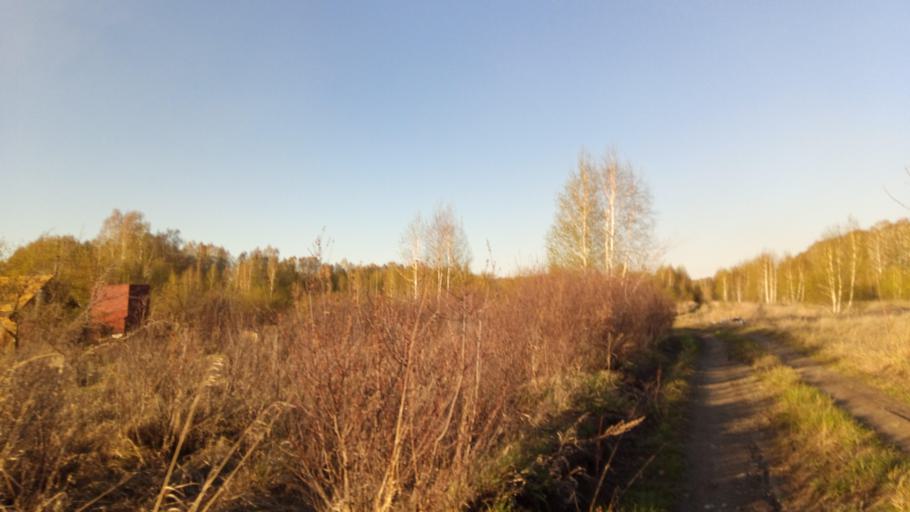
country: RU
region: Chelyabinsk
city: Timiryazevskiy
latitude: 54.9892
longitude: 60.8566
